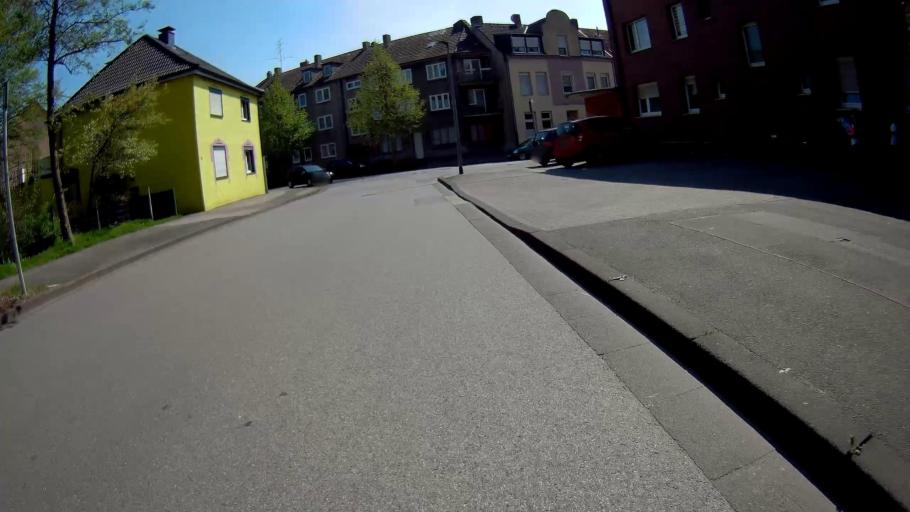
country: DE
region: North Rhine-Westphalia
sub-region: Regierungsbezirk Munster
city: Gladbeck
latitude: 51.5471
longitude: 7.0471
